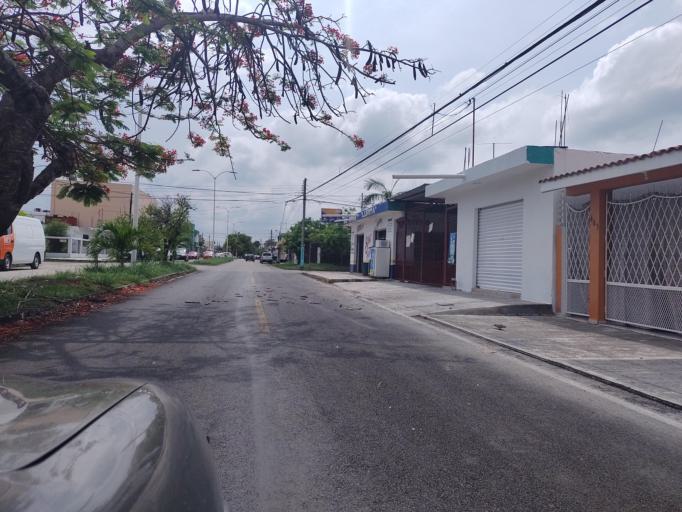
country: MX
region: Quintana Roo
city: Chetumal
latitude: 18.5164
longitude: -88.3074
